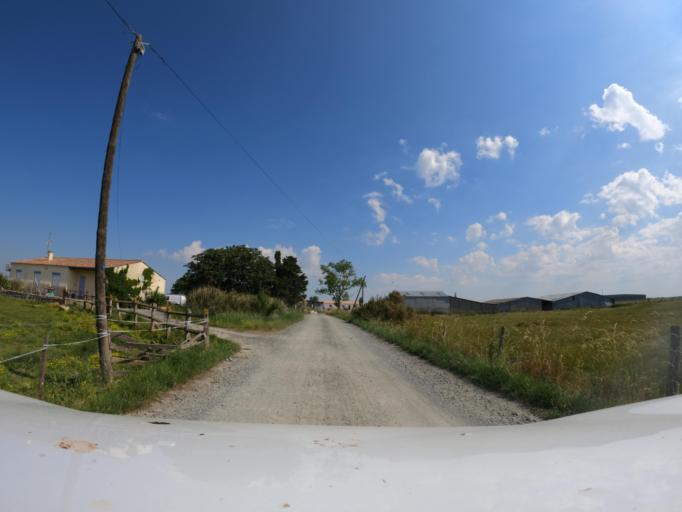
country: FR
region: Pays de la Loire
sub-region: Departement de la Vendee
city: Champagne-les-Marais
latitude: 46.3846
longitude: -1.1072
